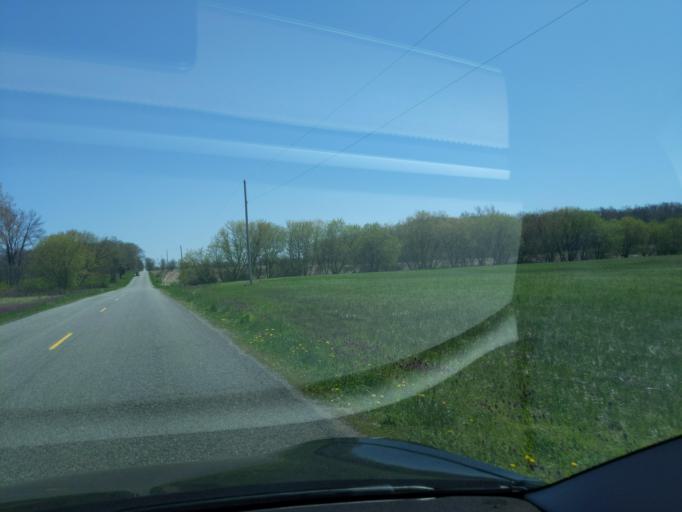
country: US
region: Michigan
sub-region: Eaton County
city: Eaton Rapids
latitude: 42.5531
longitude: -84.5791
